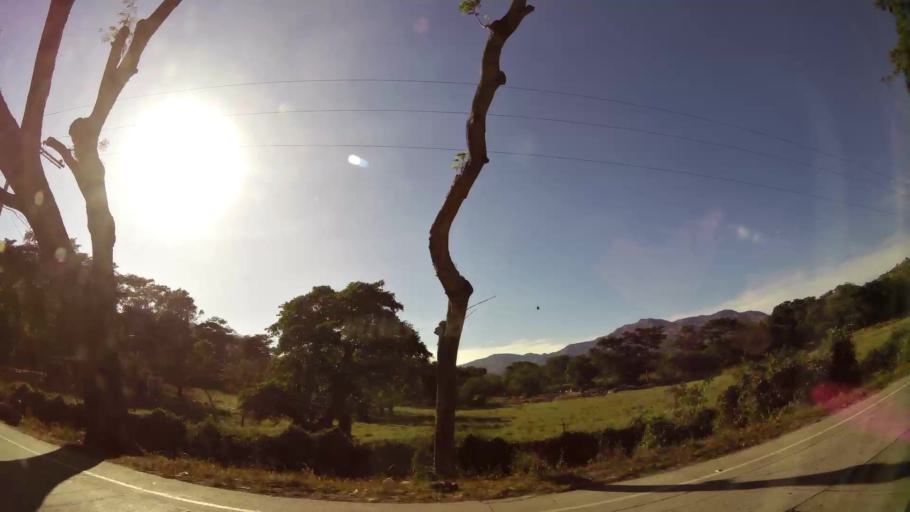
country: SV
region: Santa Ana
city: Texistepeque
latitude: 14.0691
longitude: -89.5027
